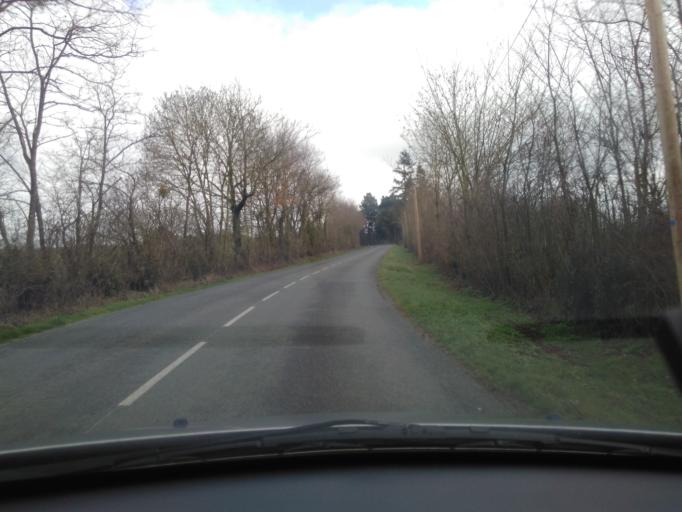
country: FR
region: Pays de la Loire
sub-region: Departement de la Vendee
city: Sainte-Cecile
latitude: 46.7024
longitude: -1.1229
